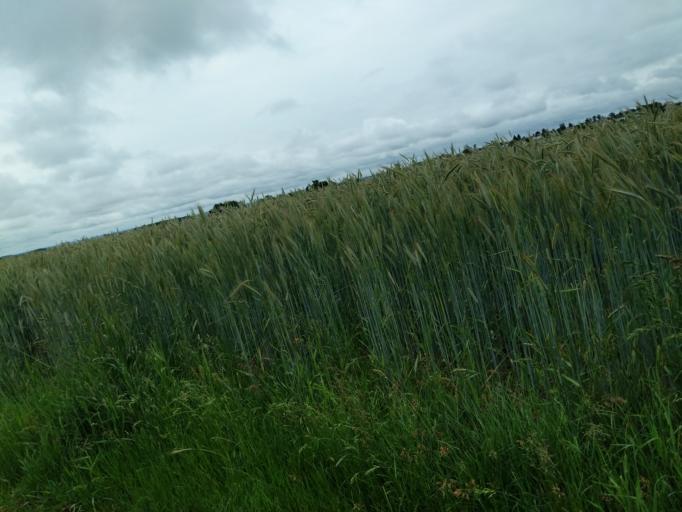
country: DE
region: Bavaria
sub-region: Upper Palatinate
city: Lappersdorf
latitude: 49.0648
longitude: 12.0805
